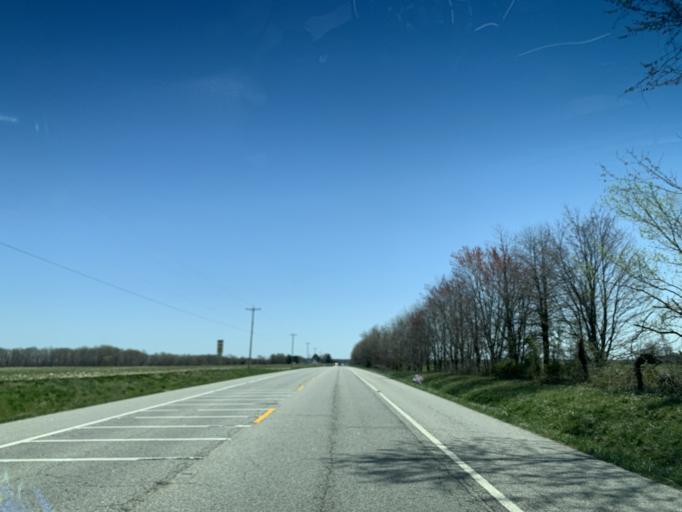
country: US
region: Maryland
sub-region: Queen Anne's County
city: Centreville
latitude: 39.0005
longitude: -76.0699
